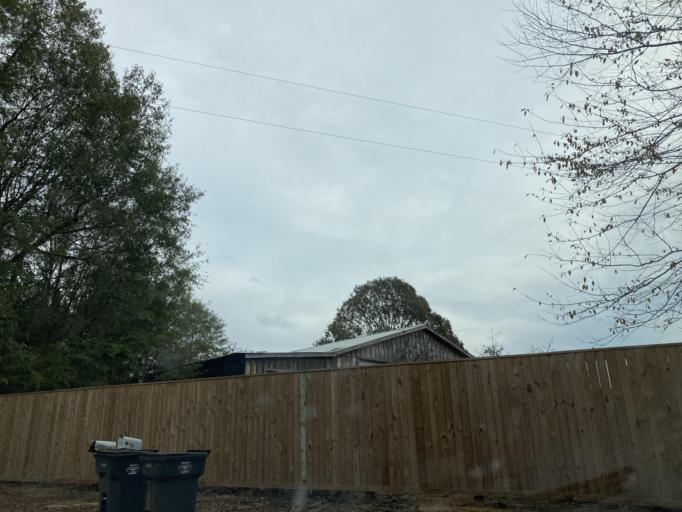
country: US
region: Mississippi
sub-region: Lamar County
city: Purvis
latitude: 31.1383
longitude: -89.4615
